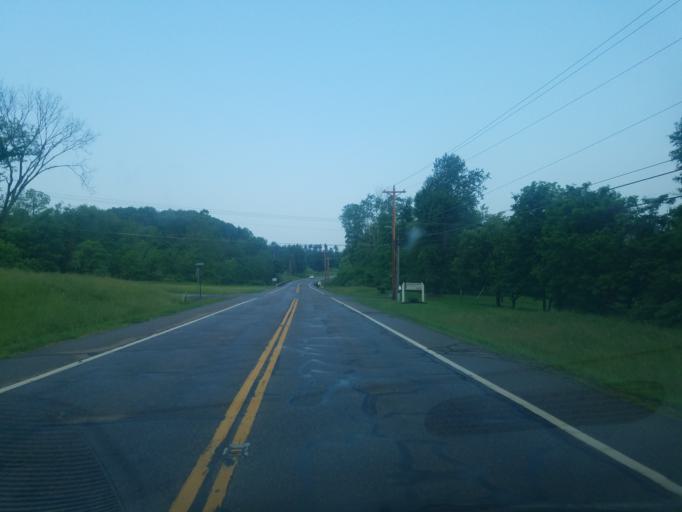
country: US
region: Ohio
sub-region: Tuscarawas County
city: Rockford
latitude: 40.5472
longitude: -81.2376
